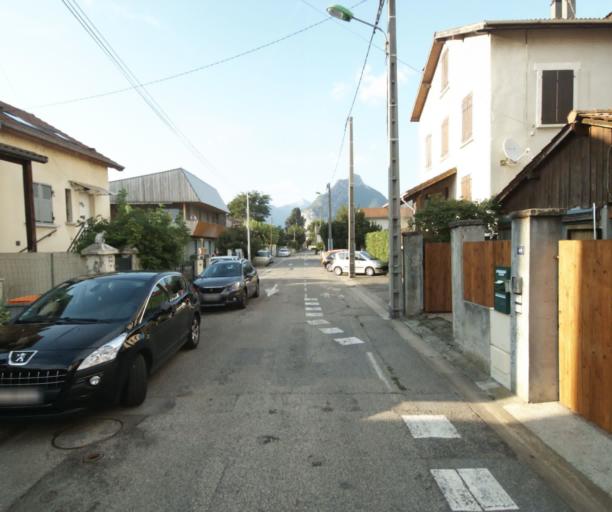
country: FR
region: Rhone-Alpes
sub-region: Departement de l'Isere
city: Seyssinet-Pariset
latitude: 45.1831
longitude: 5.6994
